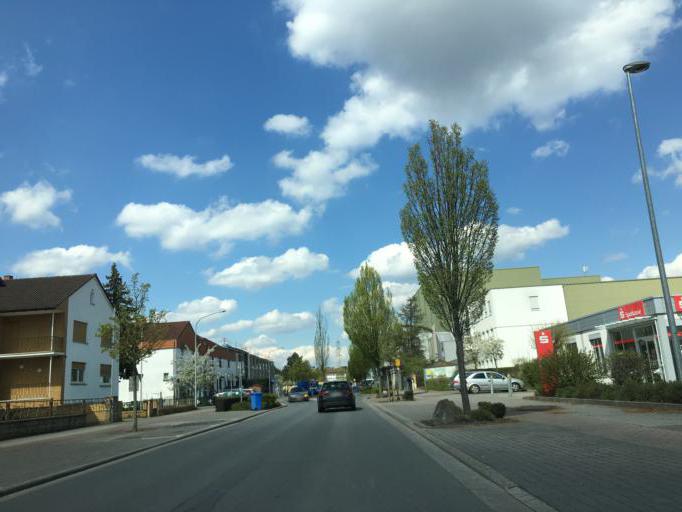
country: DE
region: Hesse
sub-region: Regierungsbezirk Darmstadt
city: Gross-Zimmern
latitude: 49.8803
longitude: 8.8196
